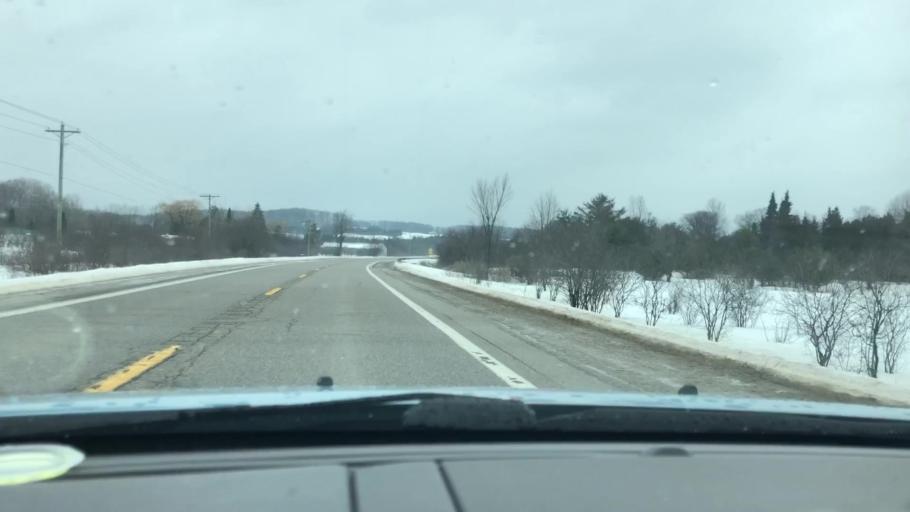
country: US
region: Michigan
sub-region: Charlevoix County
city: East Jordan
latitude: 45.1282
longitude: -85.1369
